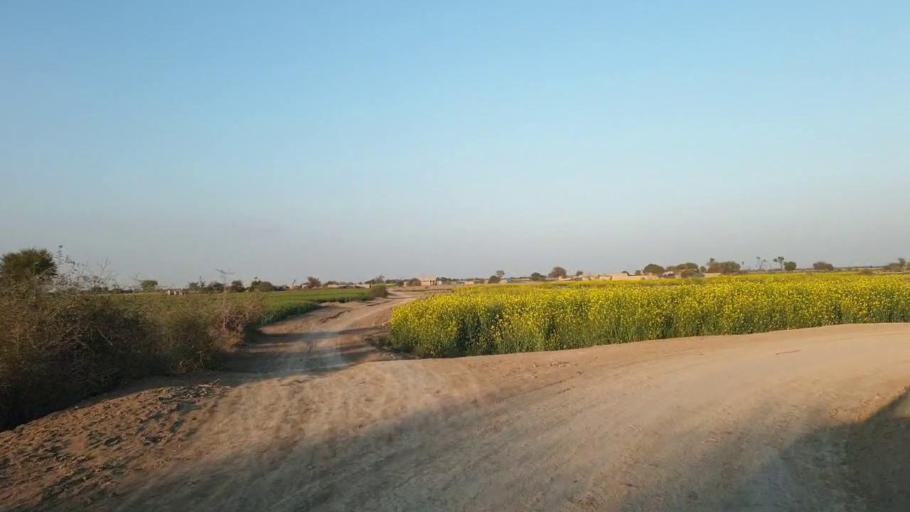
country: PK
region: Sindh
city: Shahpur Chakar
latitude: 26.1535
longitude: 68.5655
